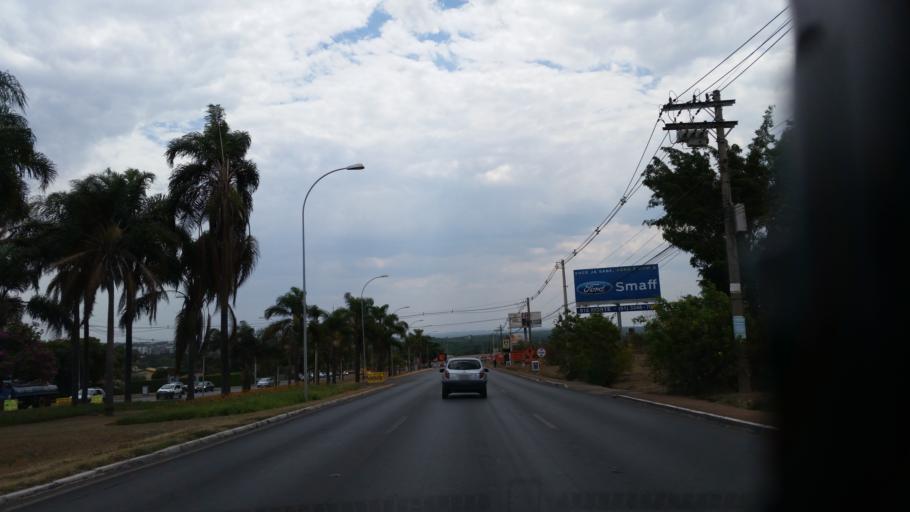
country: BR
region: Federal District
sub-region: Brasilia
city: Brasilia
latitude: -15.7228
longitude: -47.8921
